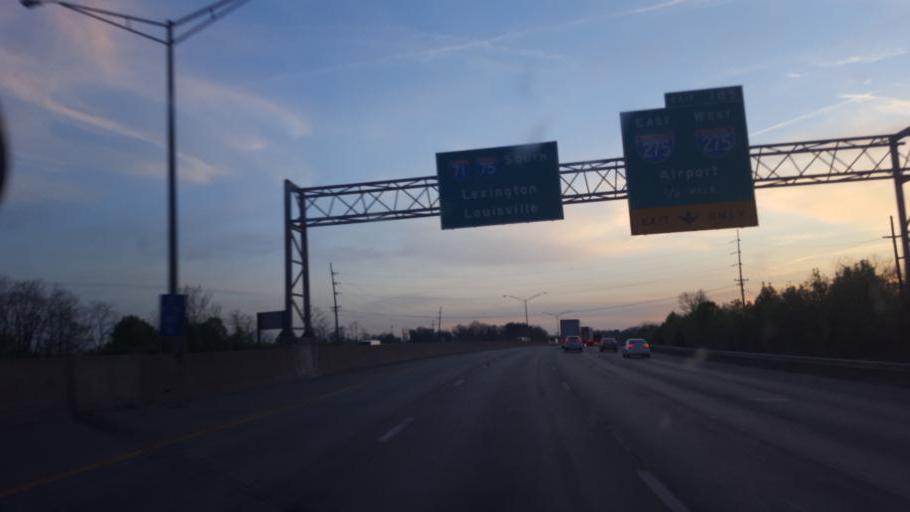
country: US
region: Kentucky
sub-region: Kenton County
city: Crescent Springs
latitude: 39.0420
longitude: -84.5822
